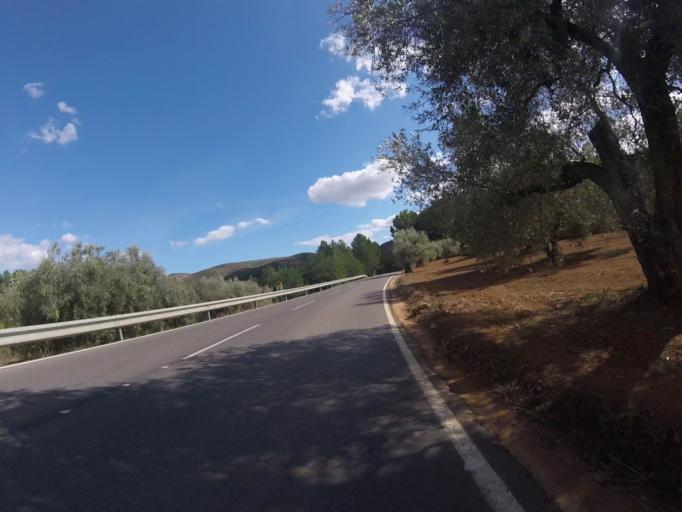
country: ES
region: Valencia
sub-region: Provincia de Castello
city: Cuevas de Vinroma
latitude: 40.3047
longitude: 0.1632
